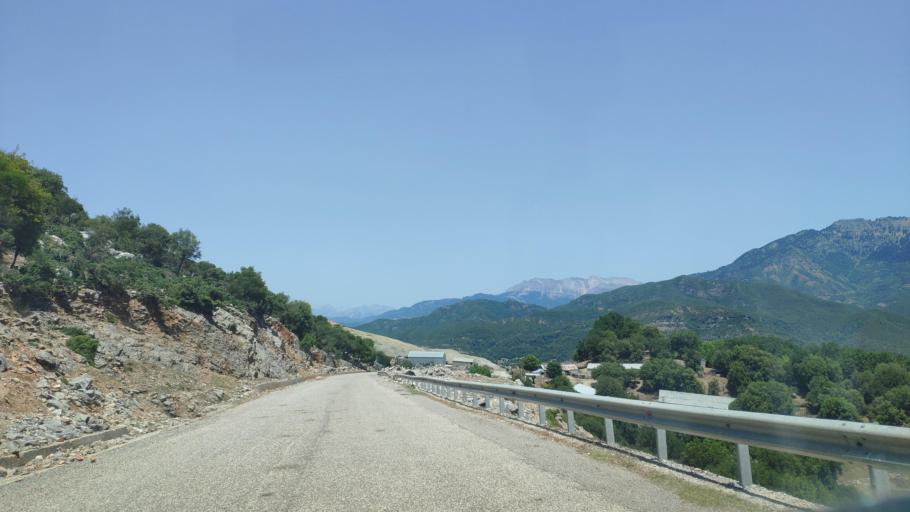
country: GR
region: Thessaly
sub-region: Nomos Kardhitsas
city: Anthiro
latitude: 39.1512
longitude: 21.3860
